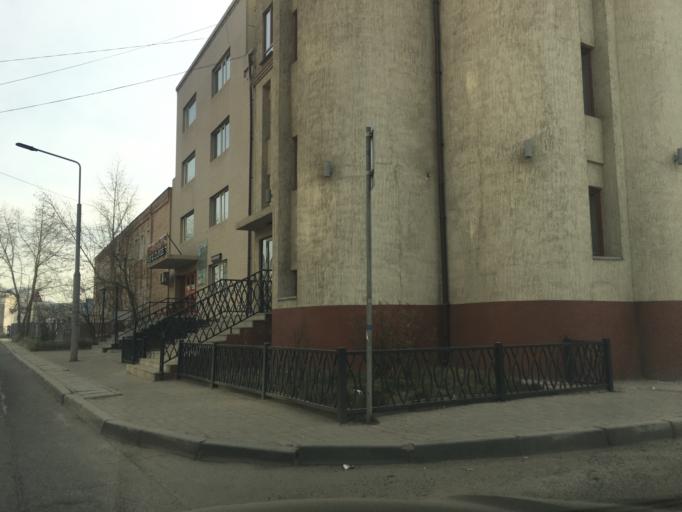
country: MN
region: Ulaanbaatar
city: Ulaanbaatar
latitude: 47.9125
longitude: 106.8894
